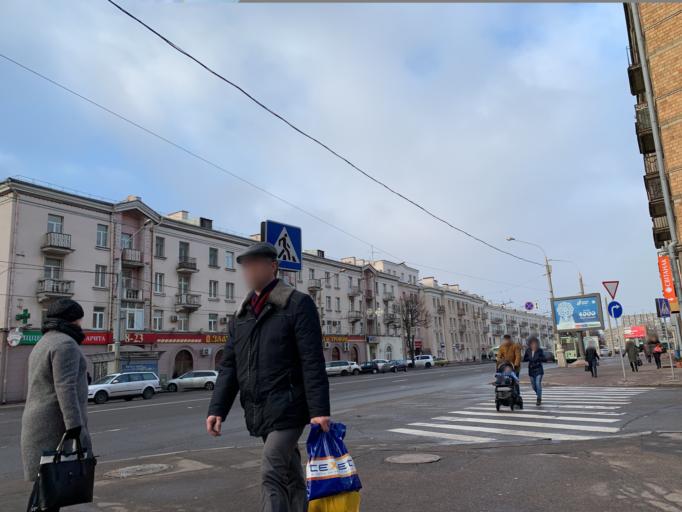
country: BY
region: Minsk
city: Minsk
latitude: 53.8888
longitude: 27.5393
